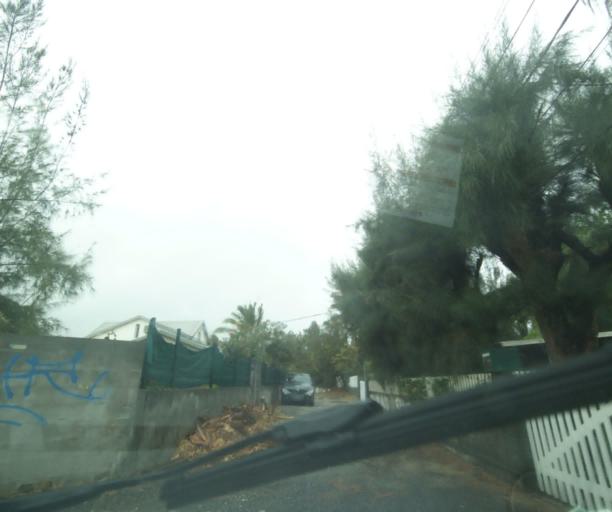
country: RE
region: Reunion
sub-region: Reunion
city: Saint-Paul
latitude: -21.0443
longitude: 55.2190
